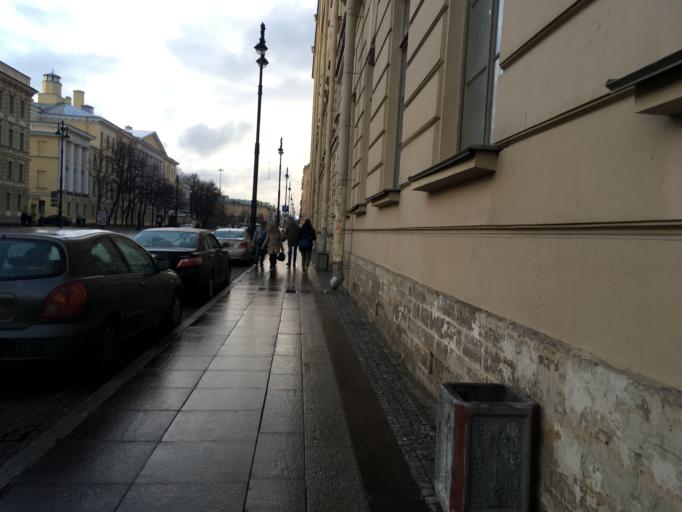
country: RU
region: St.-Petersburg
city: Saint Petersburg
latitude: 59.9182
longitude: 30.3181
